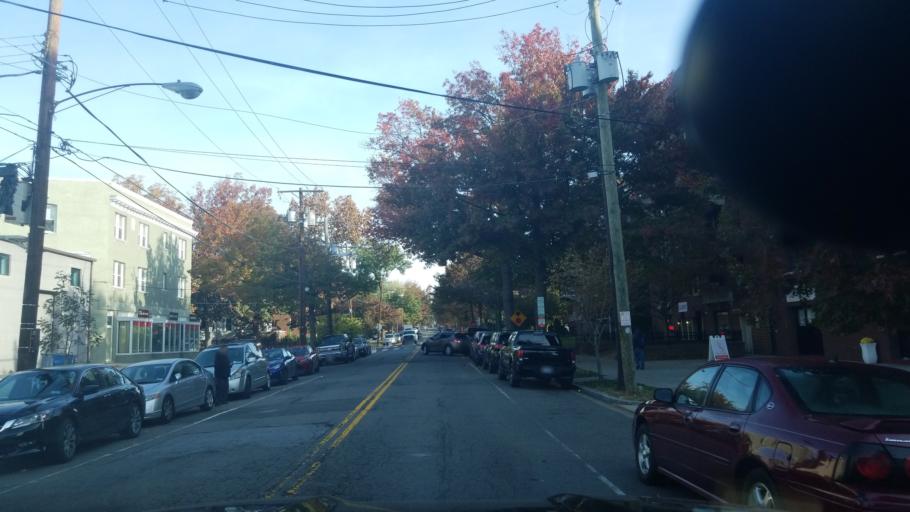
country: US
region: Maryland
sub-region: Montgomery County
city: Takoma Park
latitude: 38.9566
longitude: -77.0329
